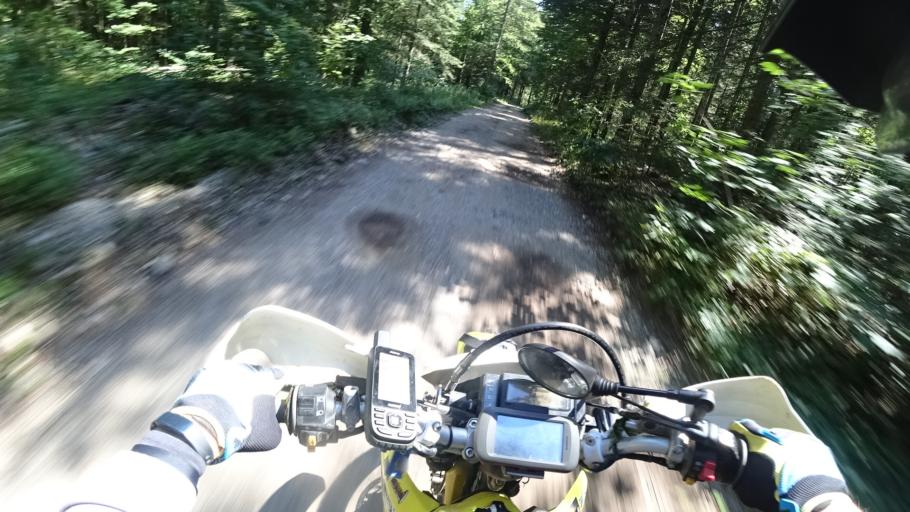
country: BA
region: Federation of Bosnia and Herzegovina
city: Orasac
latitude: 44.5030
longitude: 15.9318
